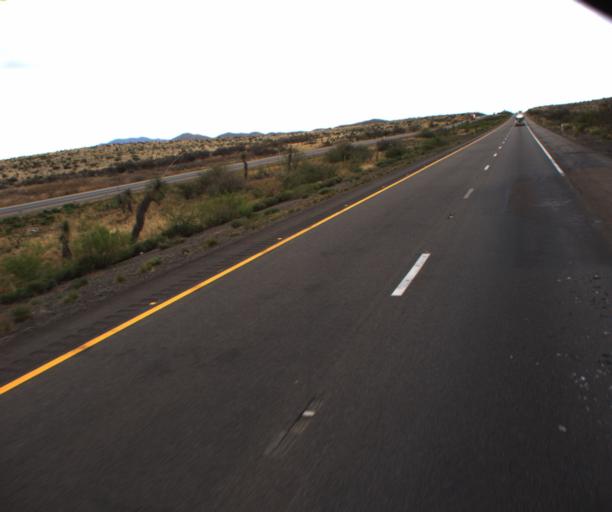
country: US
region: Arizona
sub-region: Cochise County
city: Willcox
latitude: 32.1420
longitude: -110.0004
